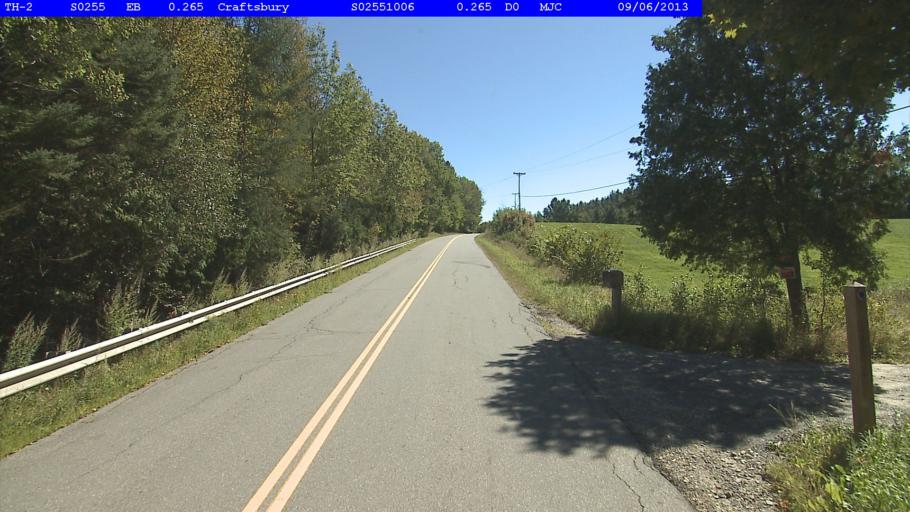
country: US
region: Vermont
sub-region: Caledonia County
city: Hardwick
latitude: 44.6279
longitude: -72.3590
